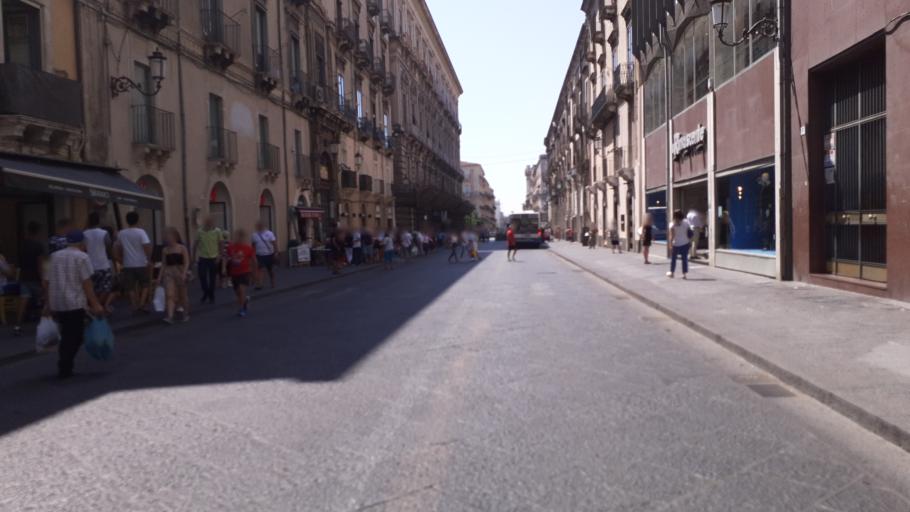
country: IT
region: Sicily
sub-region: Catania
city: Catania
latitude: 37.5089
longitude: 15.0859
